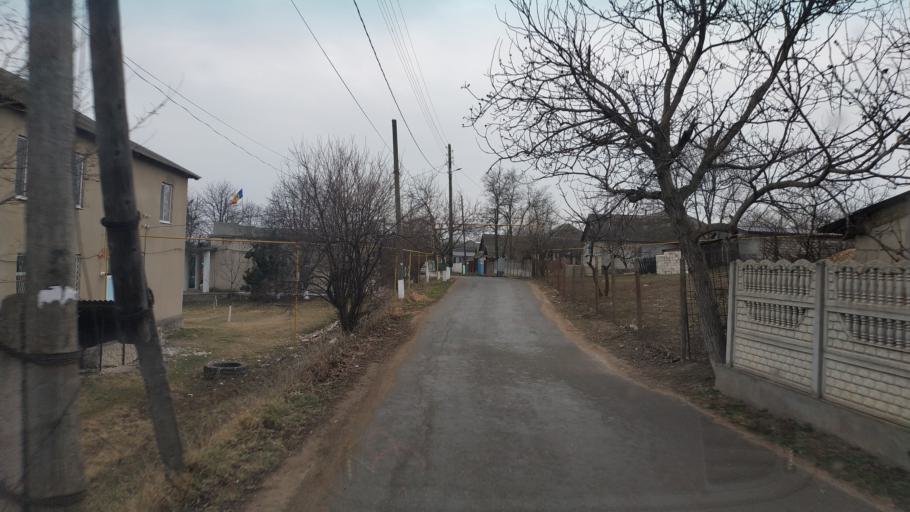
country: MD
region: Chisinau
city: Singera
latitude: 46.8278
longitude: 28.9736
